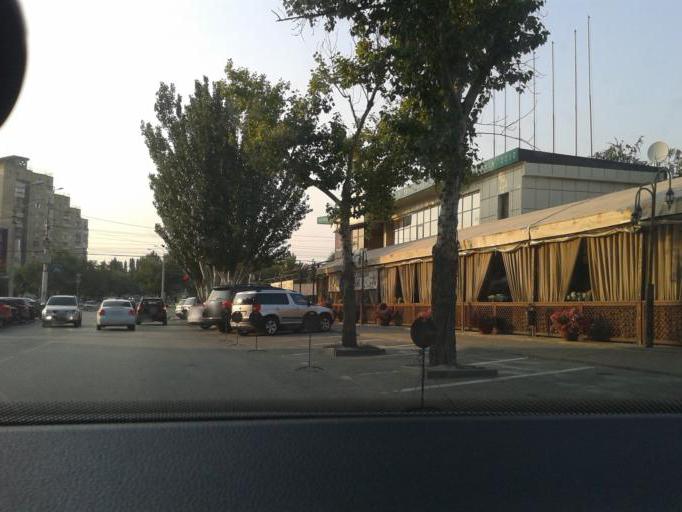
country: RU
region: Volgograd
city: Volgograd
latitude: 48.7000
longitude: 44.5064
